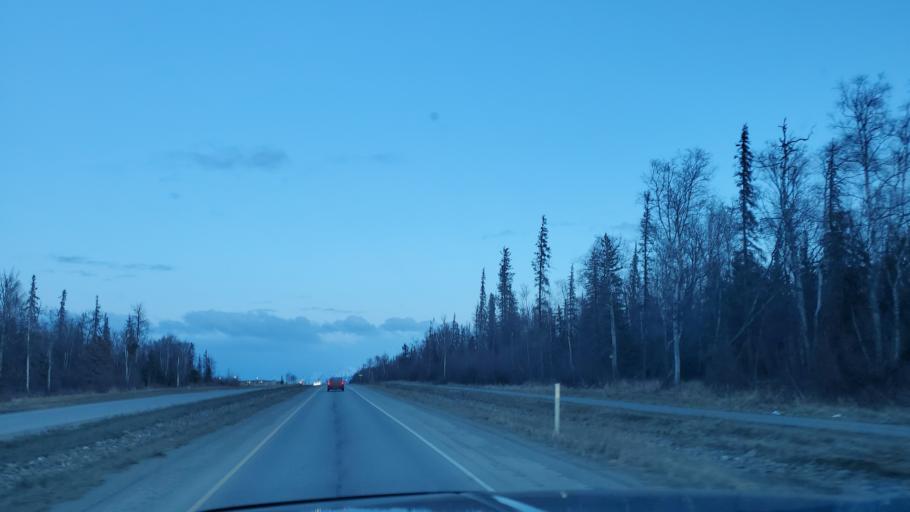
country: US
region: Alaska
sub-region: Matanuska-Susitna Borough
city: Wasilla
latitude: 61.5712
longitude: -149.4334
